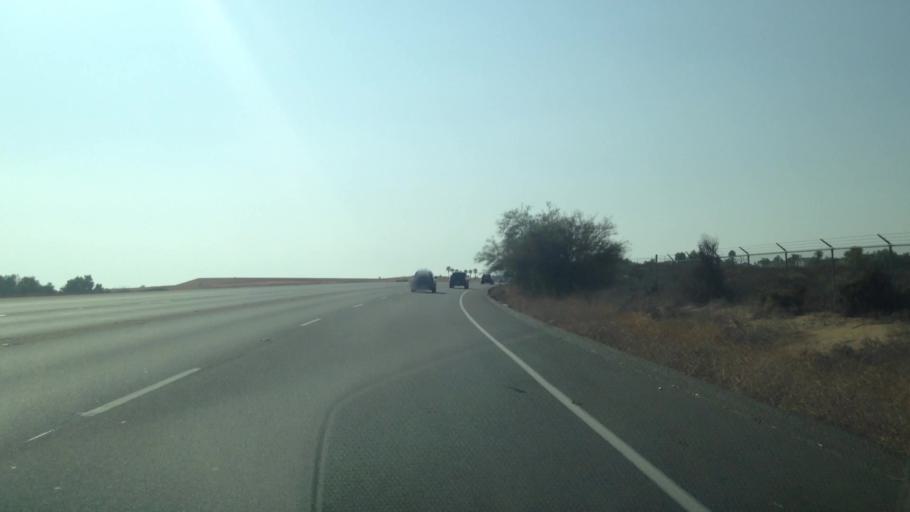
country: US
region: California
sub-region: Riverside County
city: March Air Force Base
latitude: 33.8850
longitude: -117.2946
